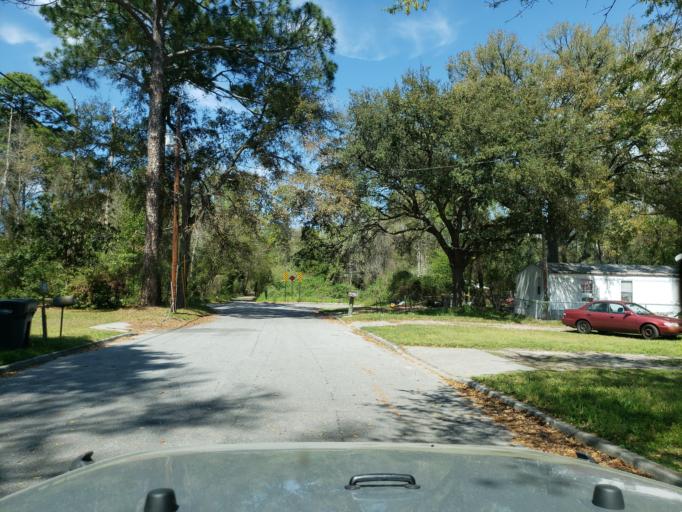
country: US
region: Georgia
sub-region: Chatham County
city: Montgomery
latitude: 31.9494
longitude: -81.1143
